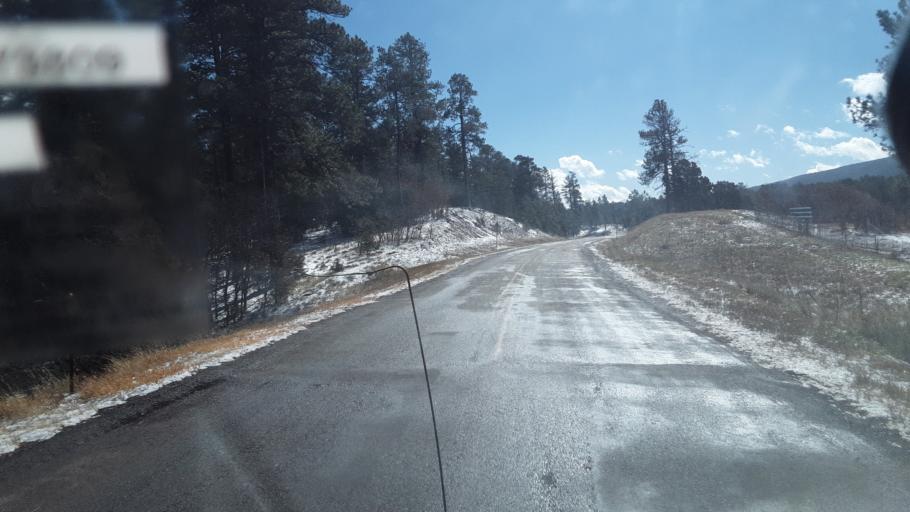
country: US
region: New Mexico
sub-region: Rio Arriba County
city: Santa Teresa
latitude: 36.2099
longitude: -106.7761
